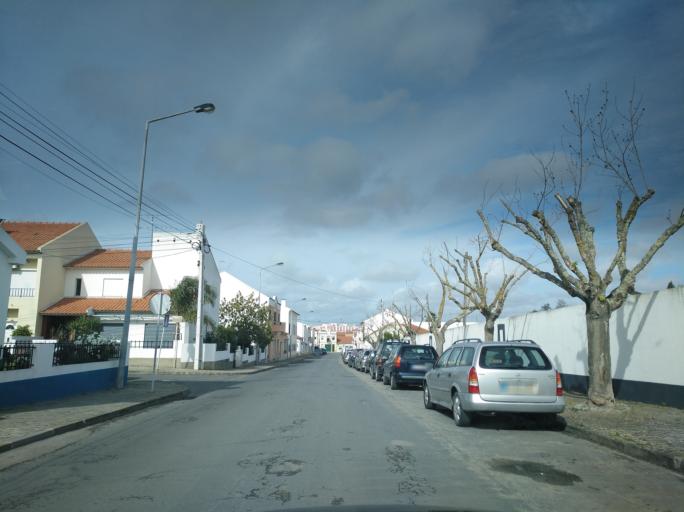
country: PT
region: Setubal
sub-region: Grandola
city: Grandola
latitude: 38.1755
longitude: -8.5614
